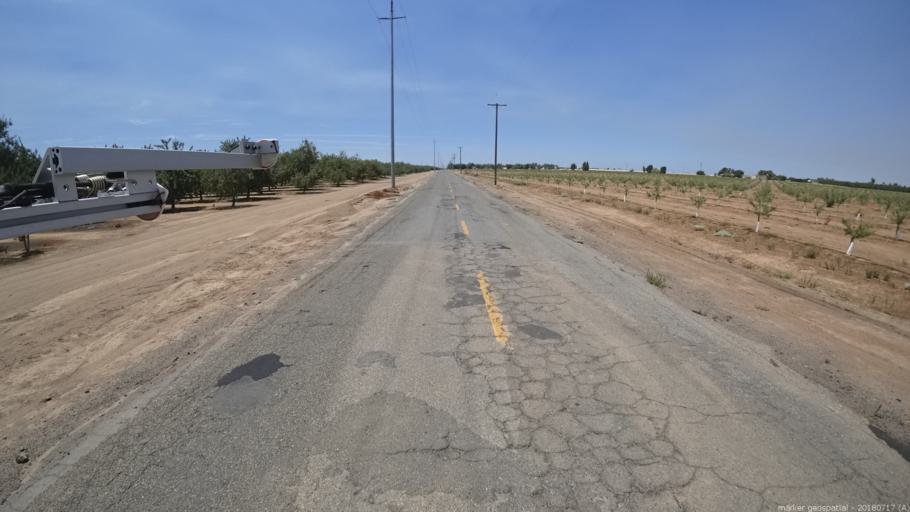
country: US
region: California
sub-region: Madera County
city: Fairmead
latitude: 37.1268
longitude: -120.1248
